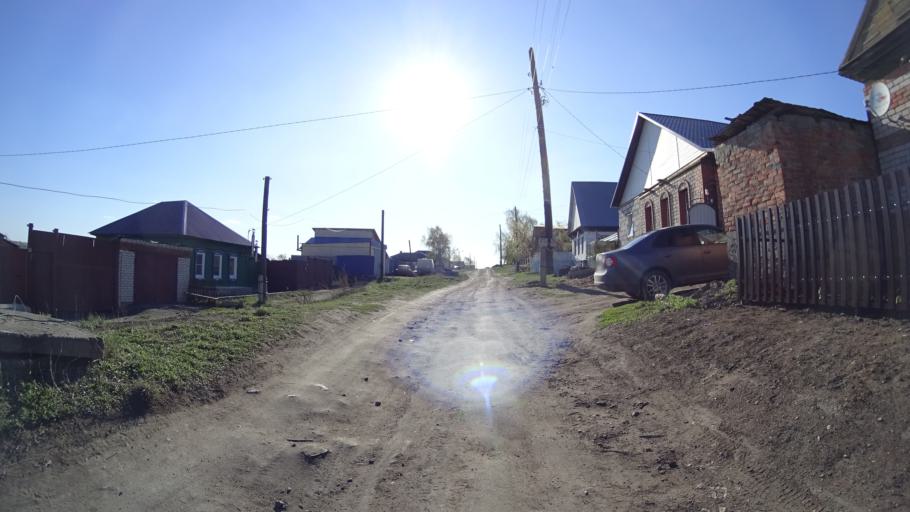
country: RU
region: Chelyabinsk
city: Troitsk
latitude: 54.0992
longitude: 61.5474
